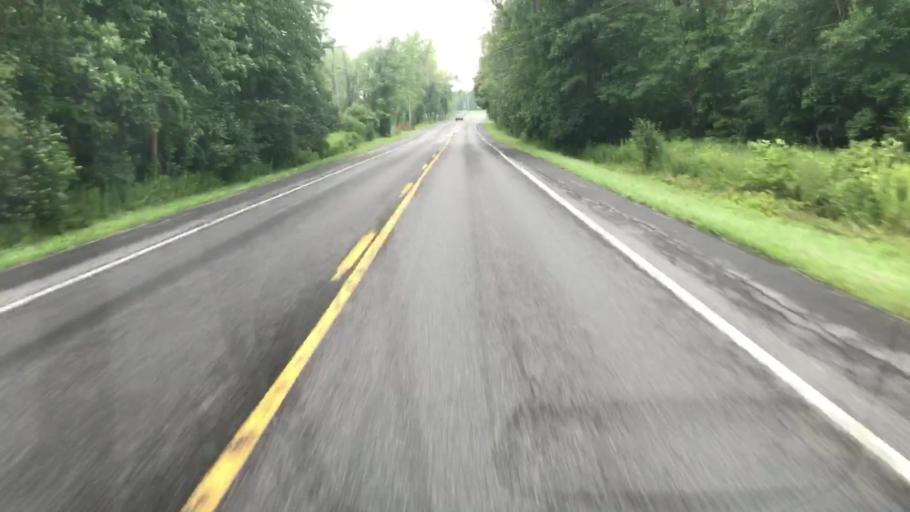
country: US
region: New York
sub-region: Onondaga County
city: Liverpool
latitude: 43.1554
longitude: -76.1917
